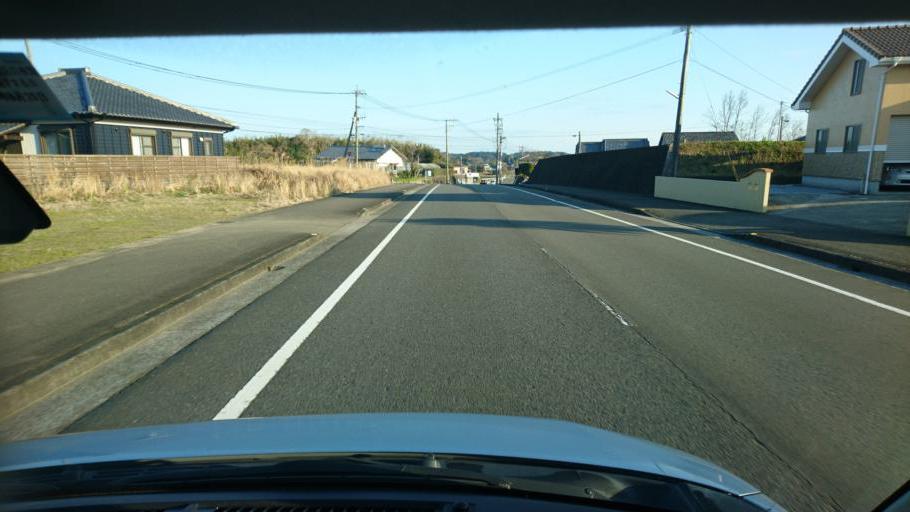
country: JP
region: Miyazaki
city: Miyazaki-shi
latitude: 31.8352
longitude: 131.4198
